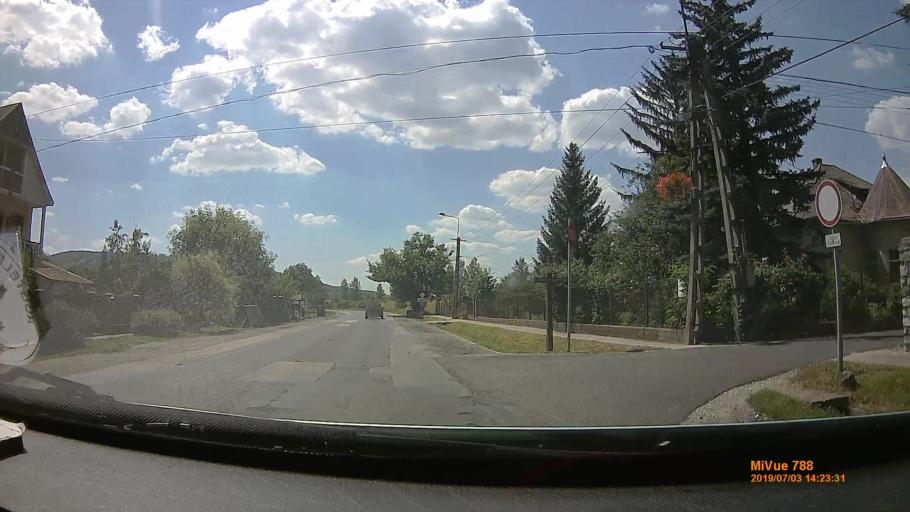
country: HU
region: Borsod-Abauj-Zemplen
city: Sajokaza
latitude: 48.2737
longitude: 20.5522
